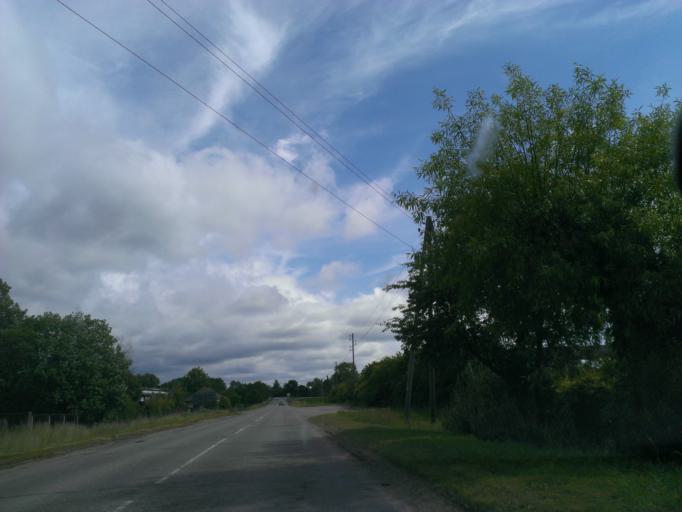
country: LV
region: Grobina
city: Grobina
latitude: 56.5370
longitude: 21.1549
